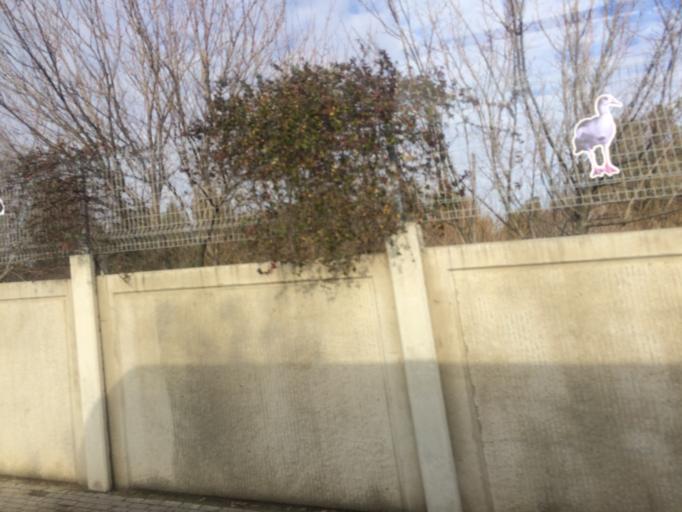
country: TR
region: Izmir
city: Karsiyaka
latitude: 38.4886
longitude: 26.9594
